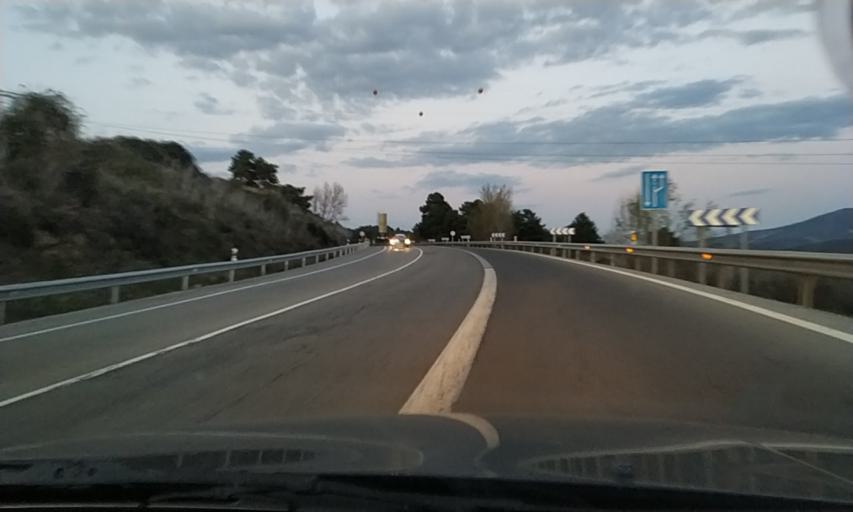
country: ES
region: Castille and Leon
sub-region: Provincia de Leon
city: Ponferrada
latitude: 42.5531
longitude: -6.5644
